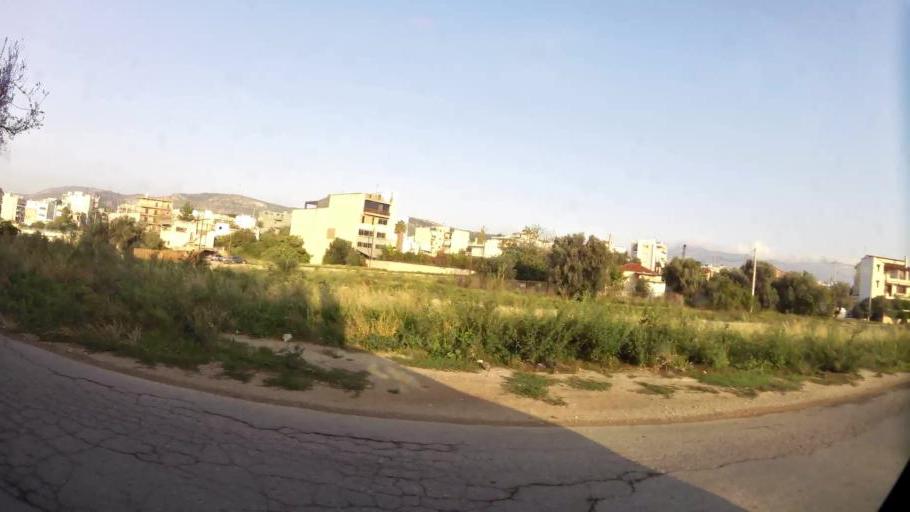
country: GR
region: Attica
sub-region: Nomarchia Dytikis Attikis
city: Zefyri
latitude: 38.0569
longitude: 23.7160
